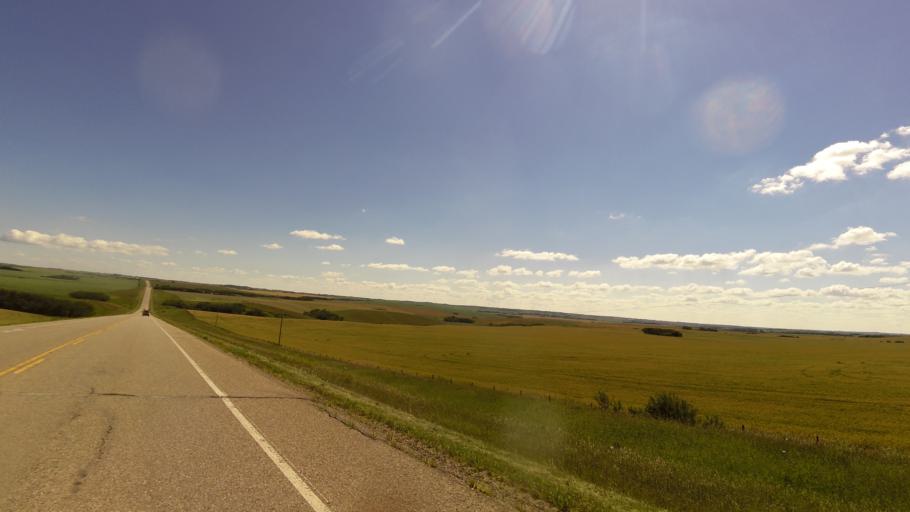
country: CA
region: Saskatchewan
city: Lloydminster
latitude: 52.8420
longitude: -110.0437
